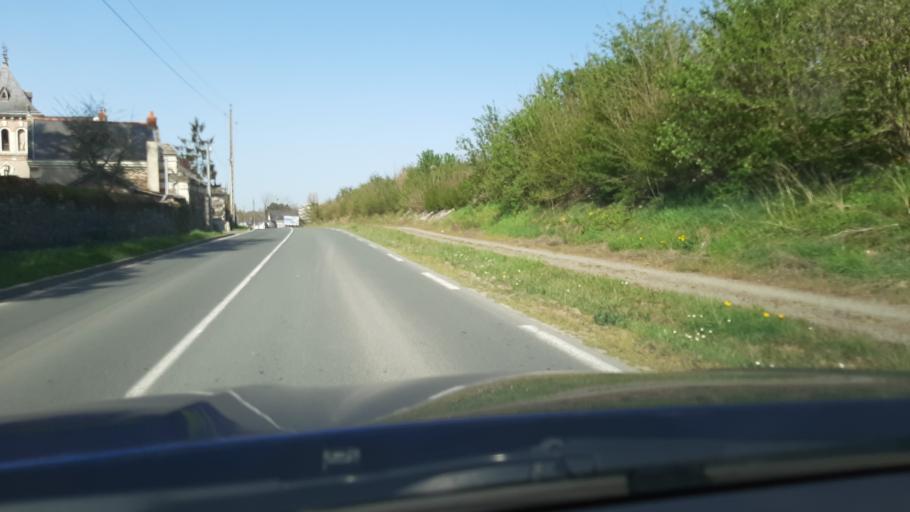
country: FR
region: Pays de la Loire
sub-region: Departement de Maine-et-Loire
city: Pellouailles-les-Vignes
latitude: 47.5134
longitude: -0.4536
